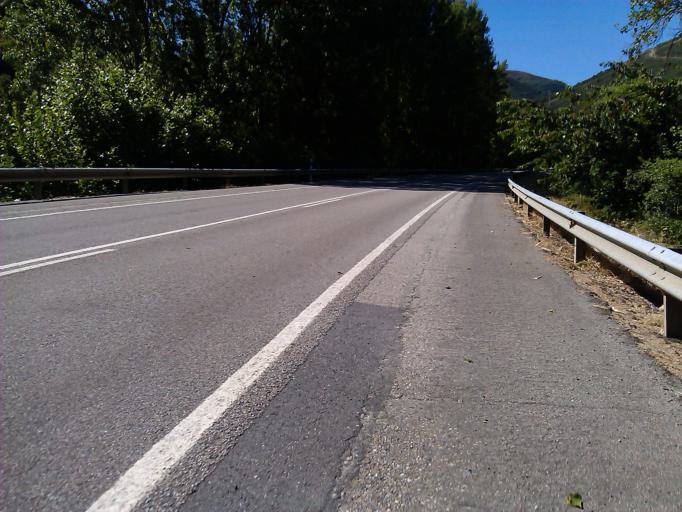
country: ES
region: Castille and Leon
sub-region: Provincia de Leon
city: Trabadelo
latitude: 42.6506
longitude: -6.8886
